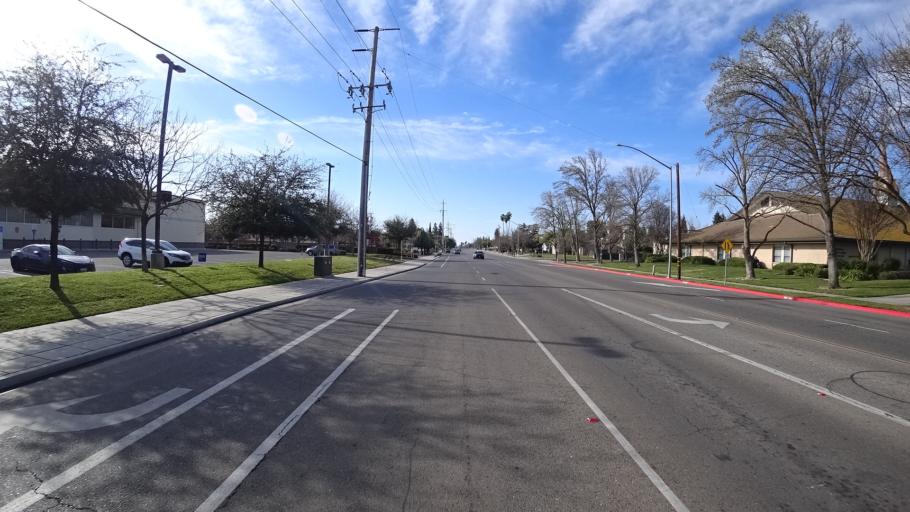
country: US
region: California
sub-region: Fresno County
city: West Park
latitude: 36.7933
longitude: -119.8804
